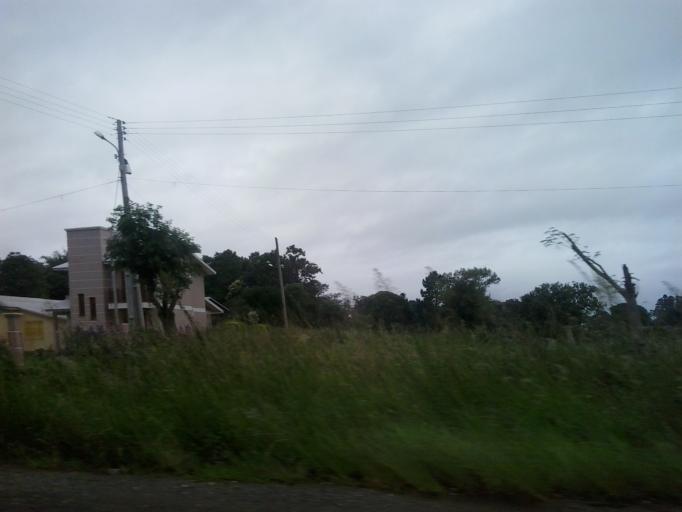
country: BR
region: Rio Grande do Sul
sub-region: Santa Maria
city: Santa Maria
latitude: -29.7222
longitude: -53.3768
